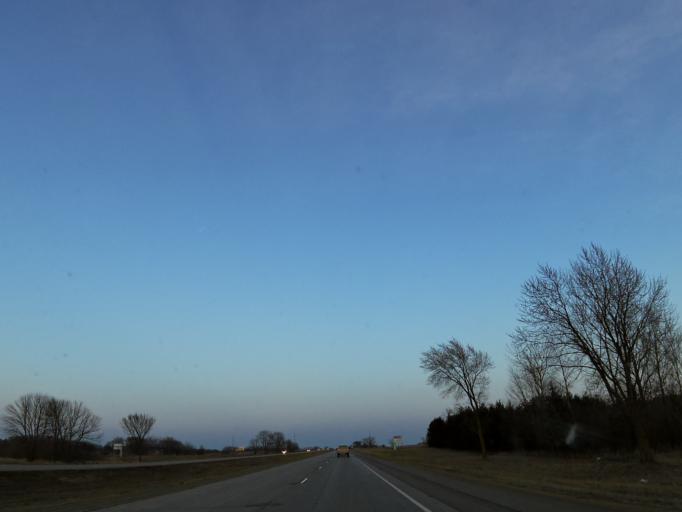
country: US
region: Minnesota
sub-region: Mower County
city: Austin
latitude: 43.6713
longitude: -92.9065
